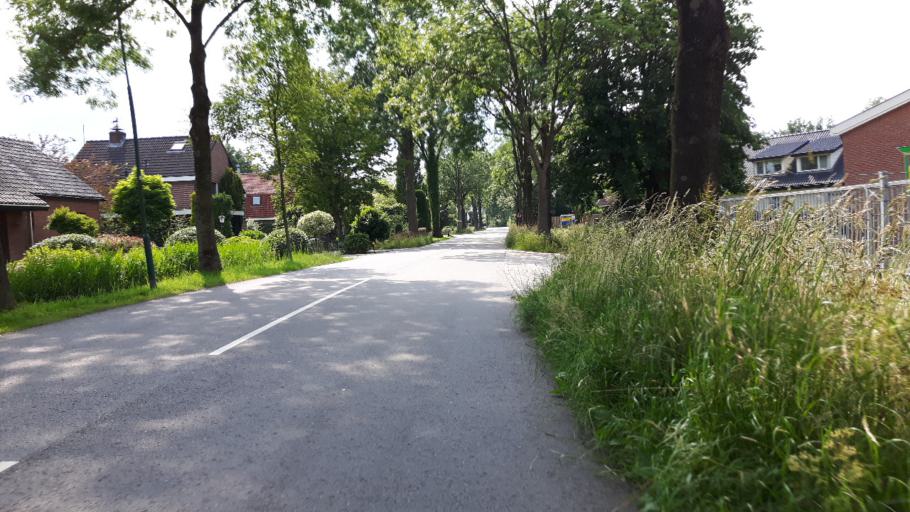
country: NL
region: Utrecht
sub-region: Gemeente Montfoort
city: Montfoort
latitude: 52.1003
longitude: 4.9471
